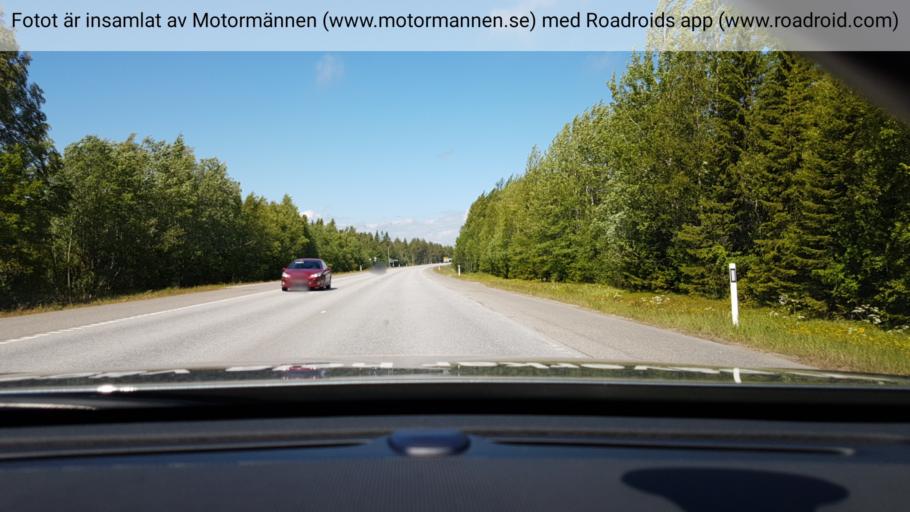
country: SE
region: Vaesterbotten
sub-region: Umea Kommun
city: Holmsund
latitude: 63.7498
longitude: 20.3731
